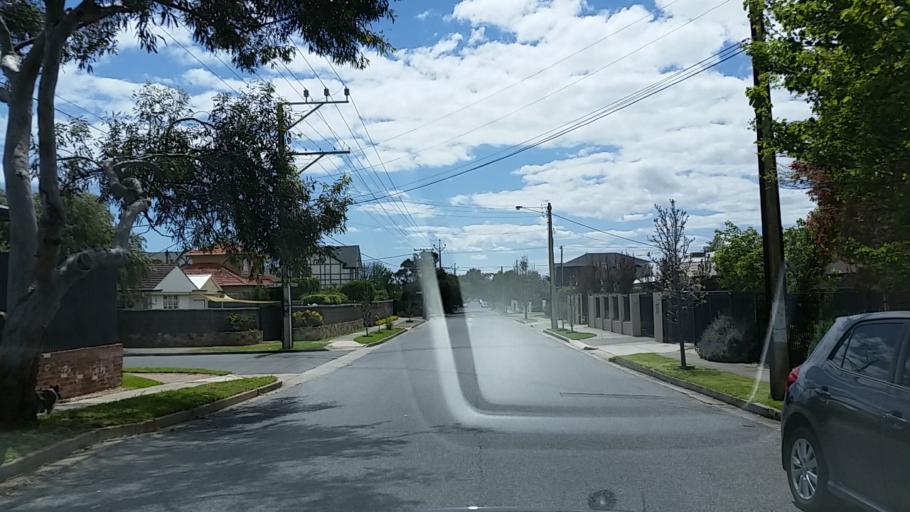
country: AU
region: South Australia
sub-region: Holdfast Bay
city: North Brighton
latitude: -34.9955
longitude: 138.5163
